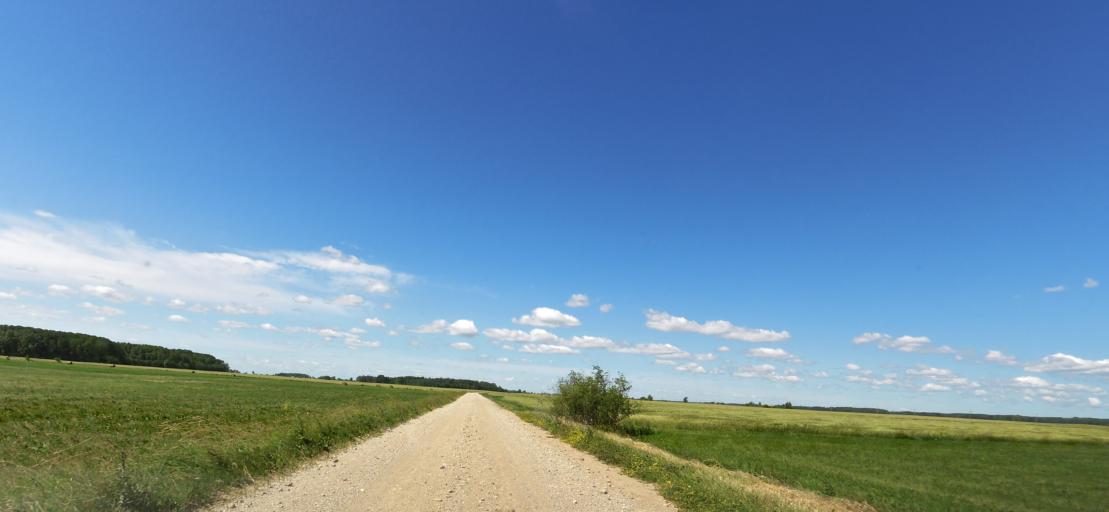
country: LT
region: Panevezys
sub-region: Birzai
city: Birzai
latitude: 56.2602
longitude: 24.5293
